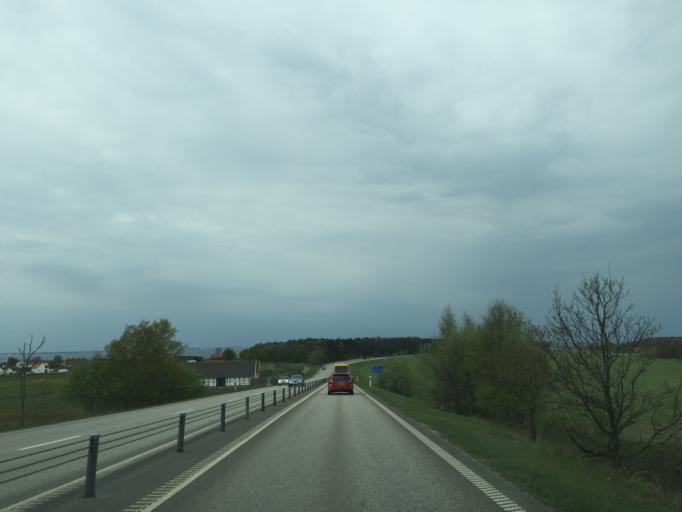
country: DK
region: Capital Region
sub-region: Helsingor Kommune
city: Hellebaek
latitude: 56.1253
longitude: 12.6106
